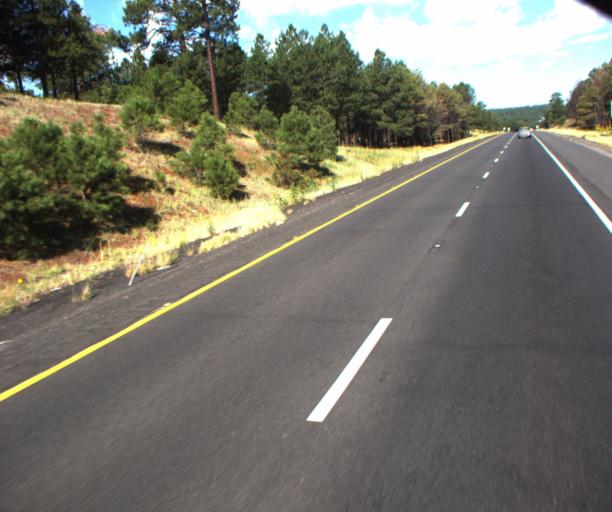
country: US
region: Arizona
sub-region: Coconino County
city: Flagstaff
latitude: 35.1824
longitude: -111.6958
